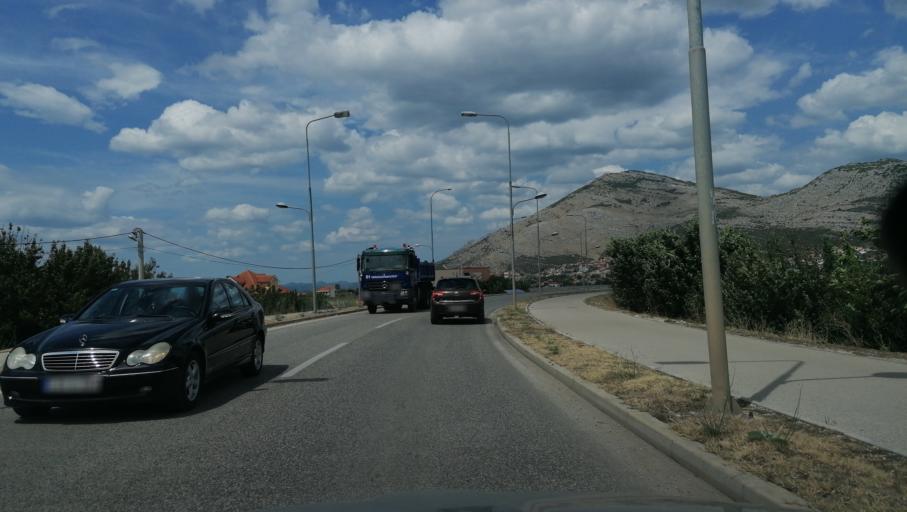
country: BA
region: Republika Srpska
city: Trebinje
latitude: 42.7001
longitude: 18.3451
